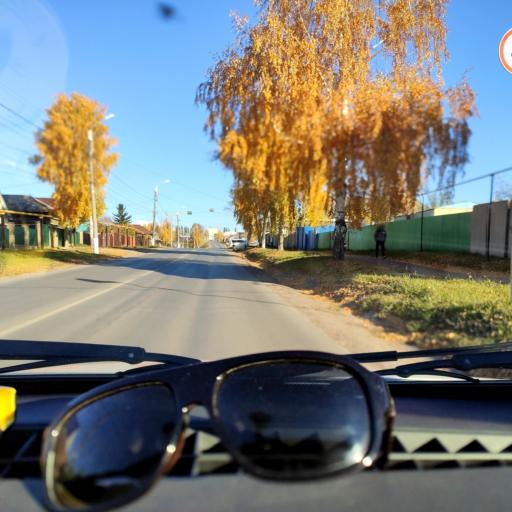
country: RU
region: Bashkortostan
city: Blagoveshchensk
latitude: 55.0390
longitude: 55.9627
